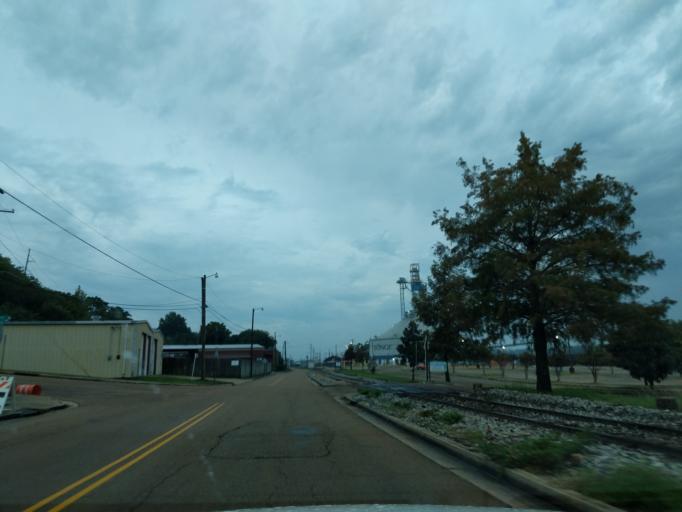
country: US
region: Mississippi
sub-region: Warren County
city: Vicksburg
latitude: 32.3488
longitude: -90.8849
